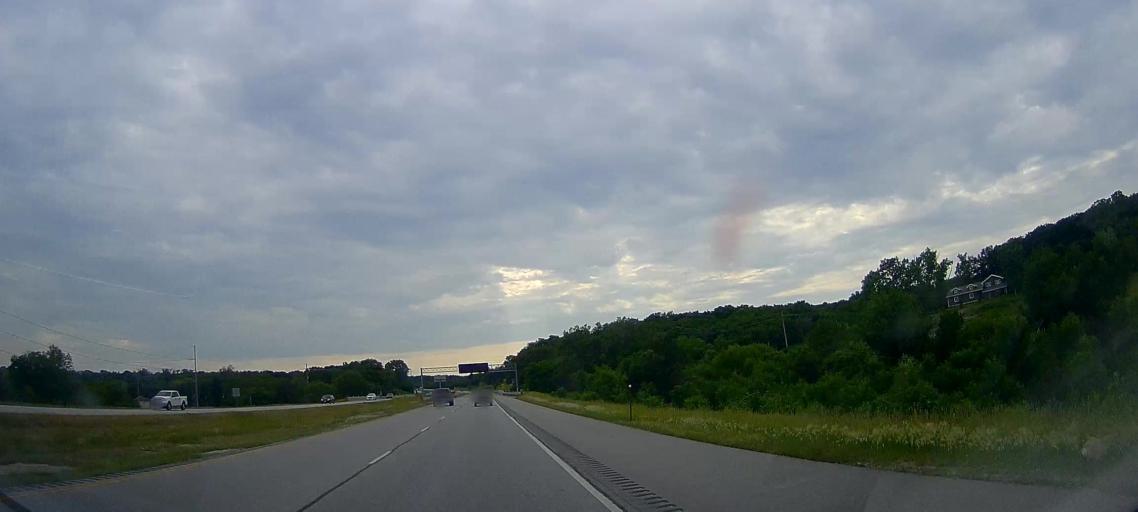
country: US
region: Iowa
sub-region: Pottawattamie County
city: Carter Lake
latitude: 41.3464
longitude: -96.0028
